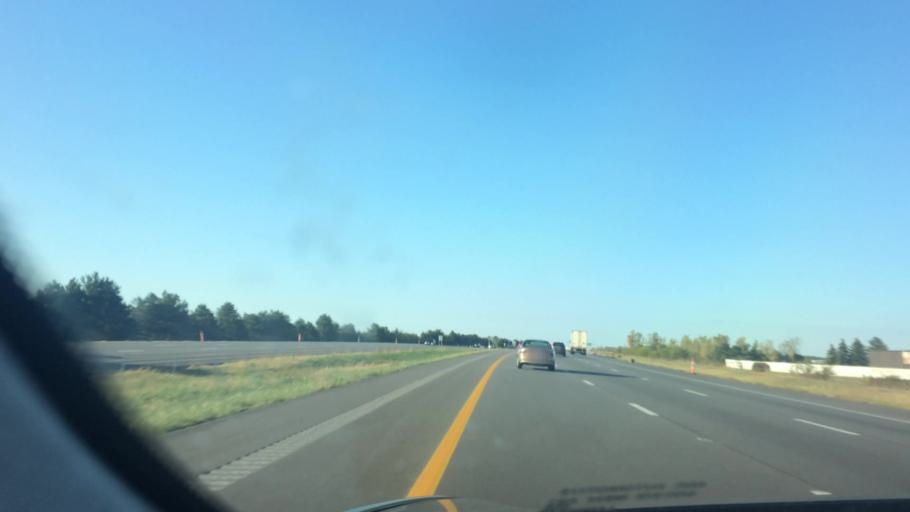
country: US
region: Ohio
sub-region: Wood County
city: Bowling Green
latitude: 41.4451
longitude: -83.6220
